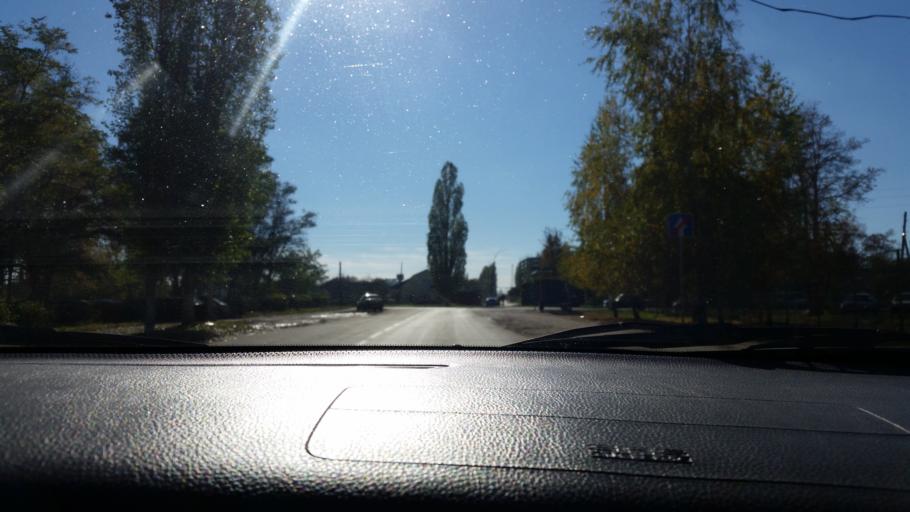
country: RU
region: Lipetsk
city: Gryazi
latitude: 52.4780
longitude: 39.9501
